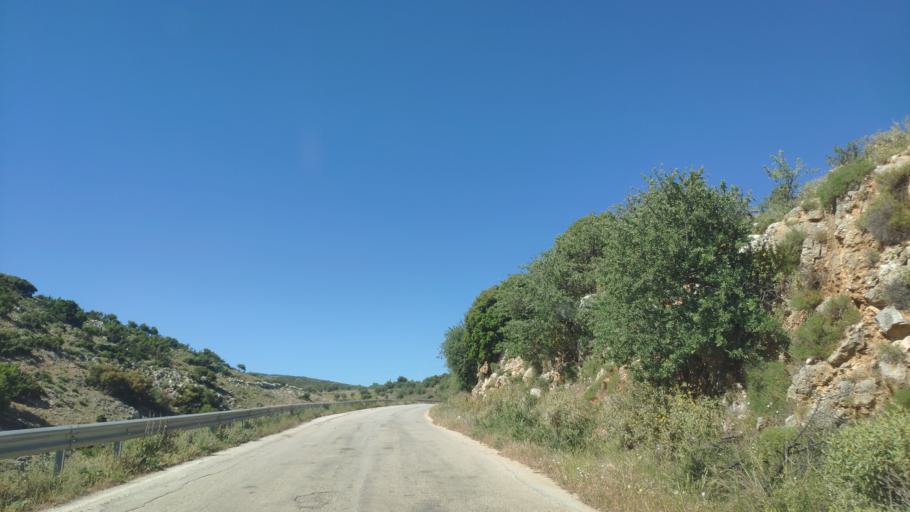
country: GR
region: Peloponnese
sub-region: Nomos Korinthias
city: Khiliomodhi
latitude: 37.7571
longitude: 22.8758
